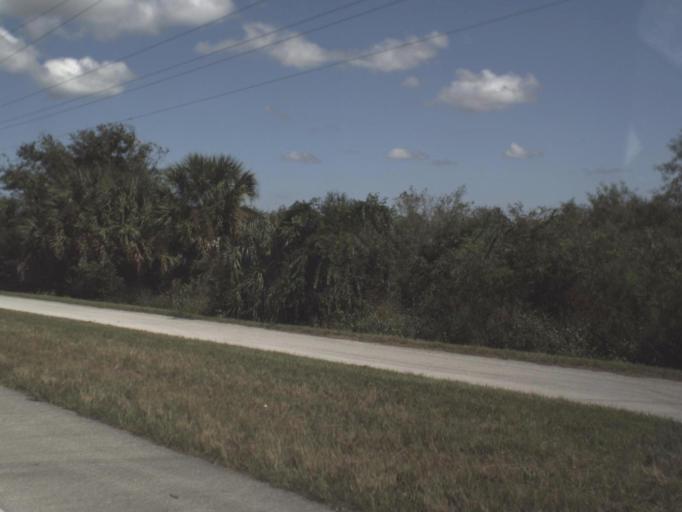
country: US
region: Florida
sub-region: Glades County
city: Moore Haven
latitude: 26.9563
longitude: -81.1221
